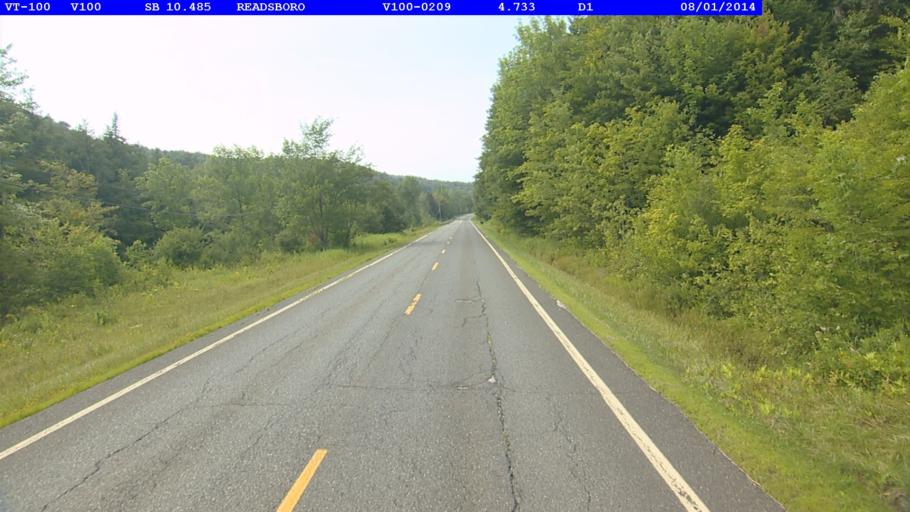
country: US
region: Massachusetts
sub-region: Berkshire County
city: North Adams
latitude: 42.7973
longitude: -72.9688
